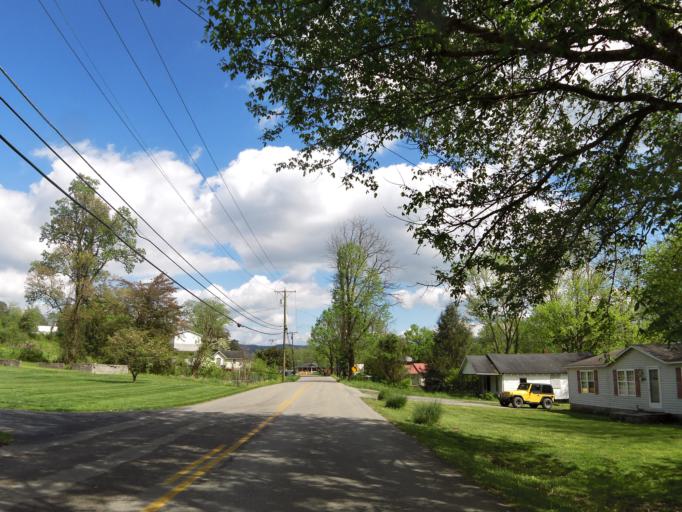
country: US
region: Kentucky
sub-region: Bell County
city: Middlesboro
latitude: 36.6162
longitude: -83.7419
